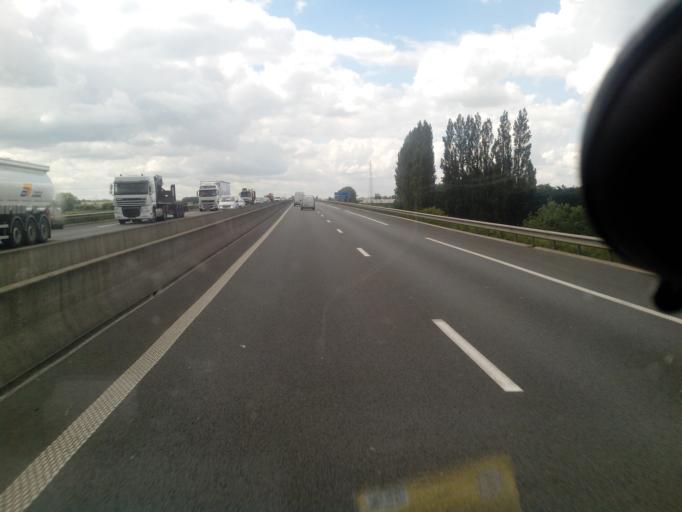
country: FR
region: Nord-Pas-de-Calais
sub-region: Departement du Nord
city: Bailleul
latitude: 50.7246
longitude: 2.7323
